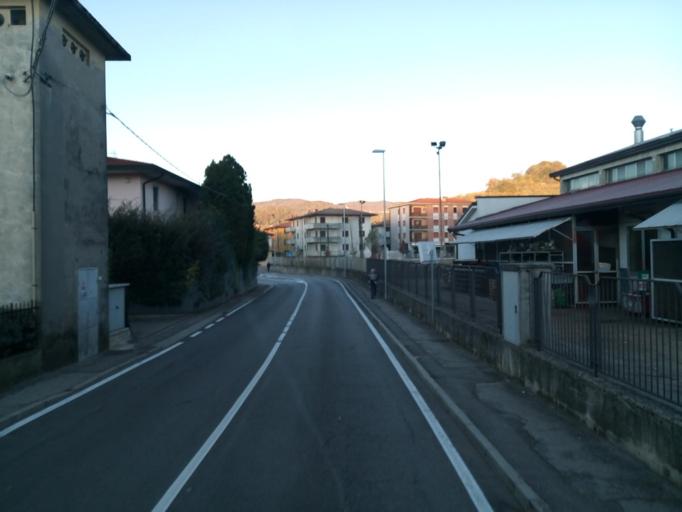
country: IT
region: Veneto
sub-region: Provincia di Vicenza
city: Trissino
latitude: 45.5622
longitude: 11.3741
